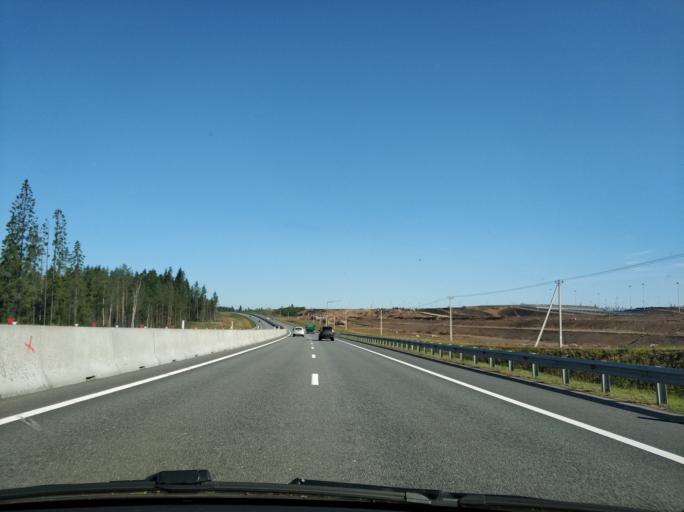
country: RU
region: Leningrad
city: Sosnovo
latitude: 60.5066
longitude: 30.1927
